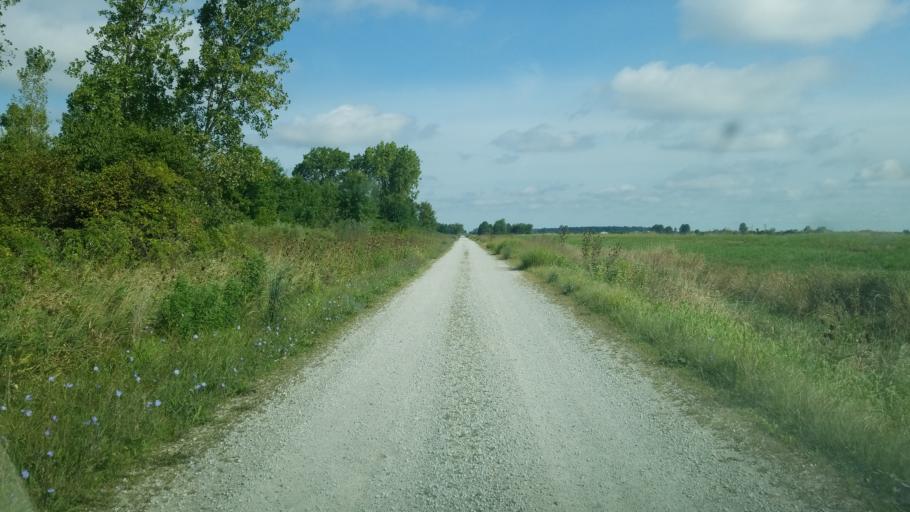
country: US
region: Ohio
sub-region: Wyandot County
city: Upper Sandusky
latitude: 40.7162
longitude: -83.3239
